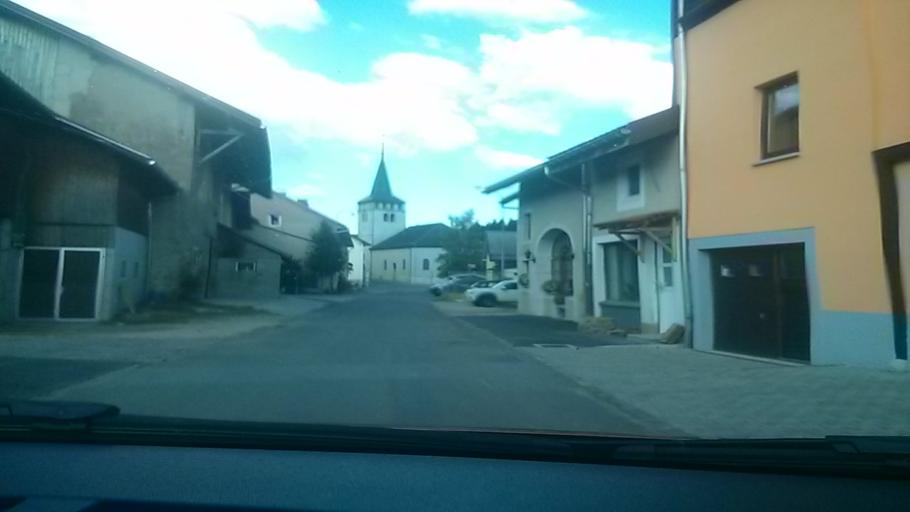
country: CH
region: Vaud
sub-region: Jura-Nord vaudois District
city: L'Abbaye
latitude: 46.6470
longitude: 6.2799
